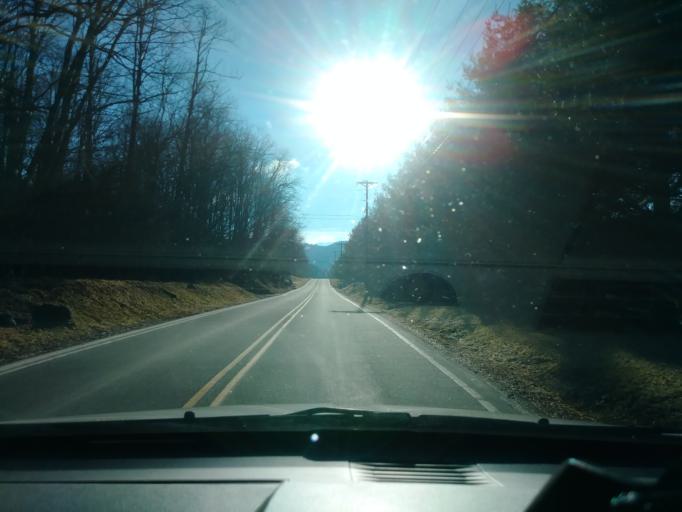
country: US
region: North Carolina
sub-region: Avery County
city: Banner Elk
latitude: 36.1636
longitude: -81.9006
